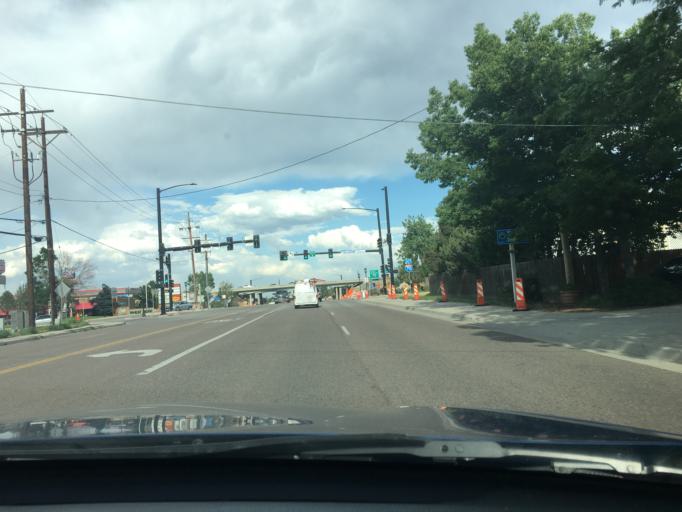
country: US
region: Colorado
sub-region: Jefferson County
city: Applewood
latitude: 39.7618
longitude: -105.1458
